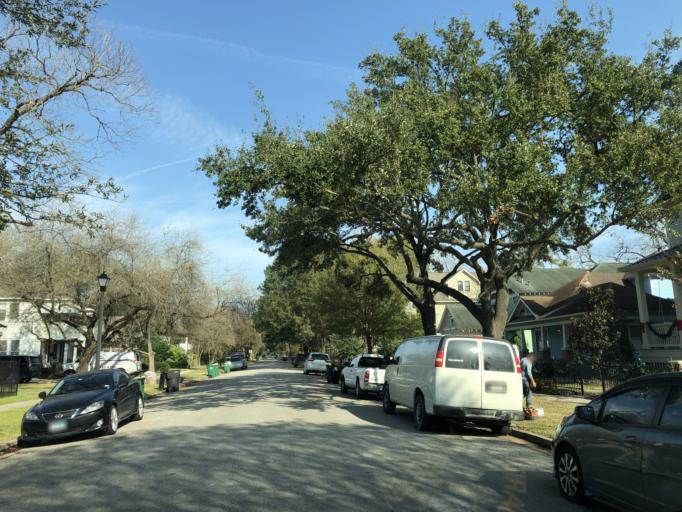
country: US
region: Texas
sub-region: Harris County
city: Houston
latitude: 29.7914
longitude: -95.3953
